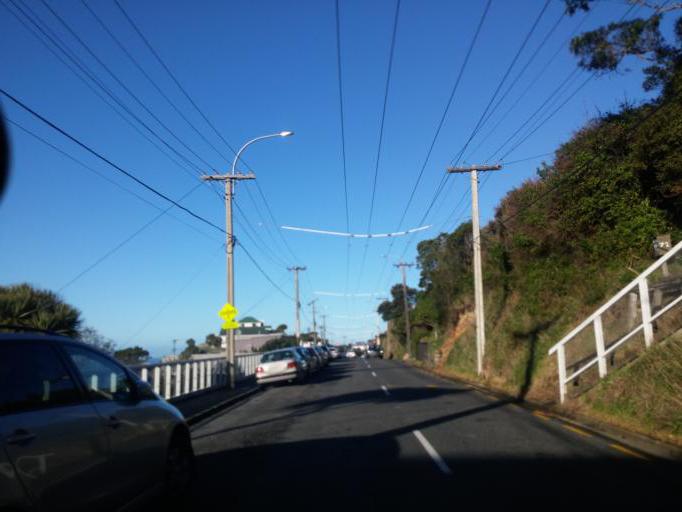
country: NZ
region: Wellington
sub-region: Wellington City
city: Brooklyn
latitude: -41.3145
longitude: 174.7655
